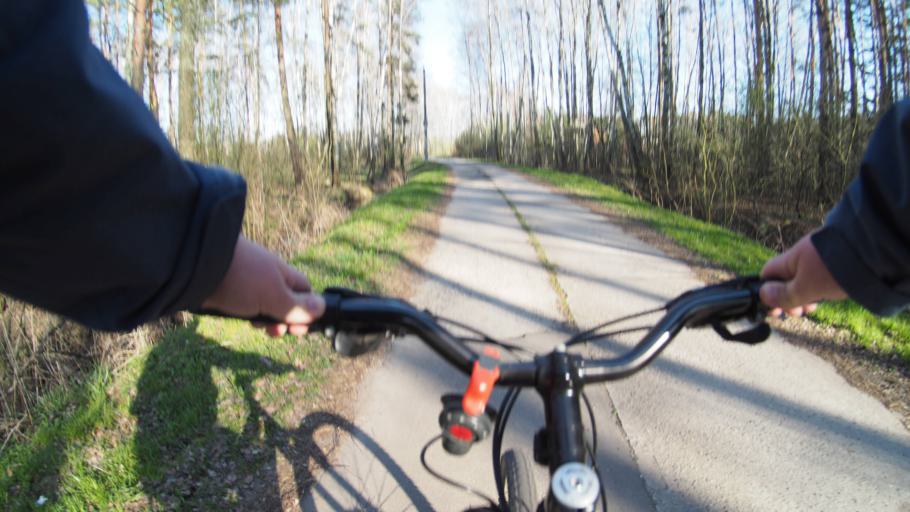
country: RU
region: Moskovskaya
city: Malyshevo
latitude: 55.5214
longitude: 38.3248
